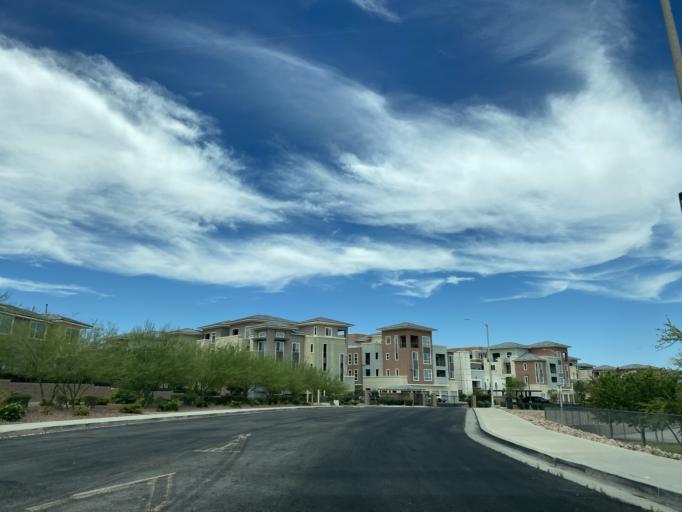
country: US
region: Nevada
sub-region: Clark County
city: Whitney
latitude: 36.0222
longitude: -115.0786
